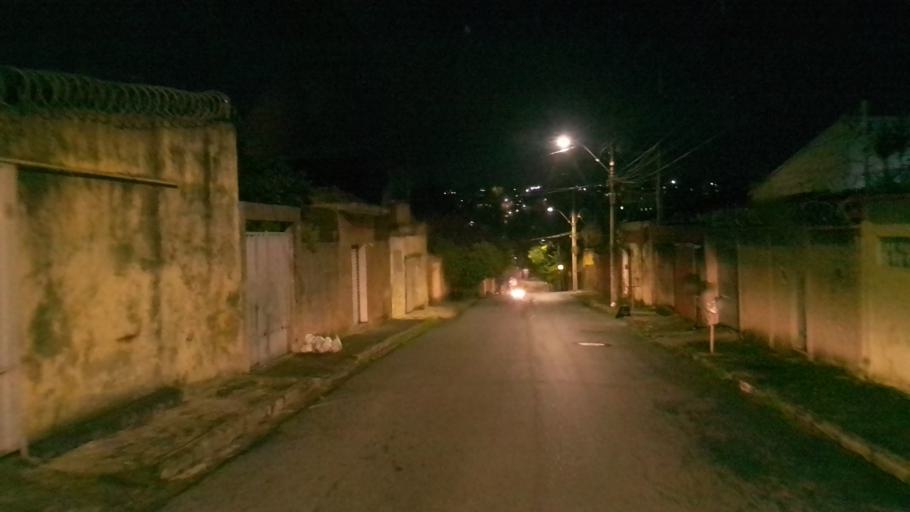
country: BR
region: Minas Gerais
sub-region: Belo Horizonte
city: Belo Horizonte
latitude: -19.8848
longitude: -43.9385
